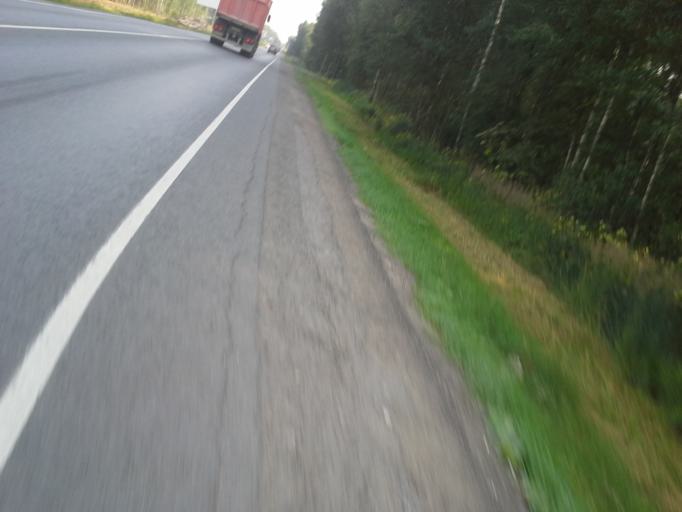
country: RU
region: Moskovskaya
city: Istra
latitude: 55.9145
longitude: 36.9454
